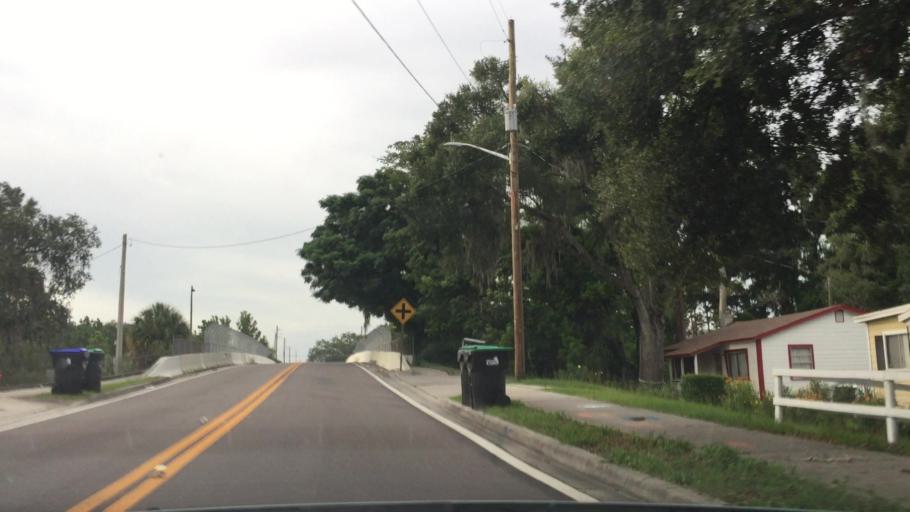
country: US
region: Florida
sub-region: Orange County
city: Orlovista
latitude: 28.5489
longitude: -81.4646
